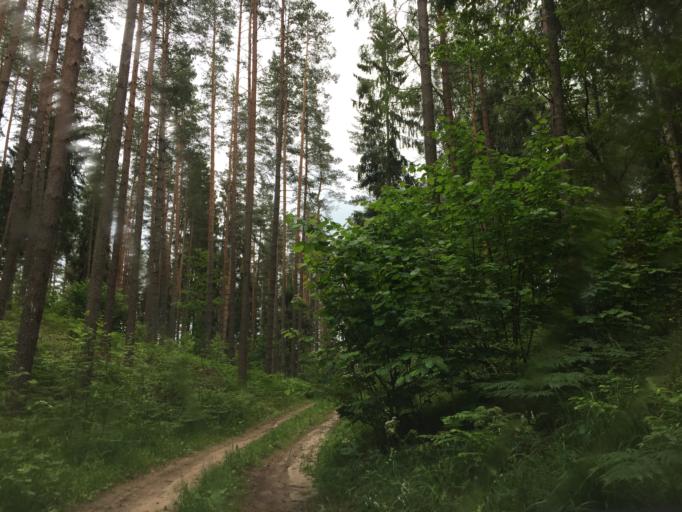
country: LV
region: Tukuma Rajons
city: Tukums
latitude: 57.0295
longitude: 23.0762
